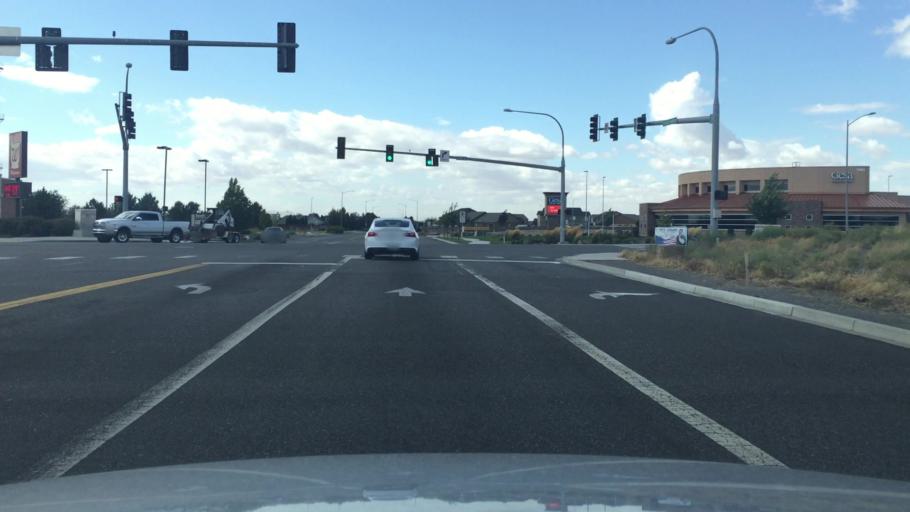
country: US
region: Washington
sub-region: Franklin County
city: West Pasco
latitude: 46.2779
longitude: -119.1859
